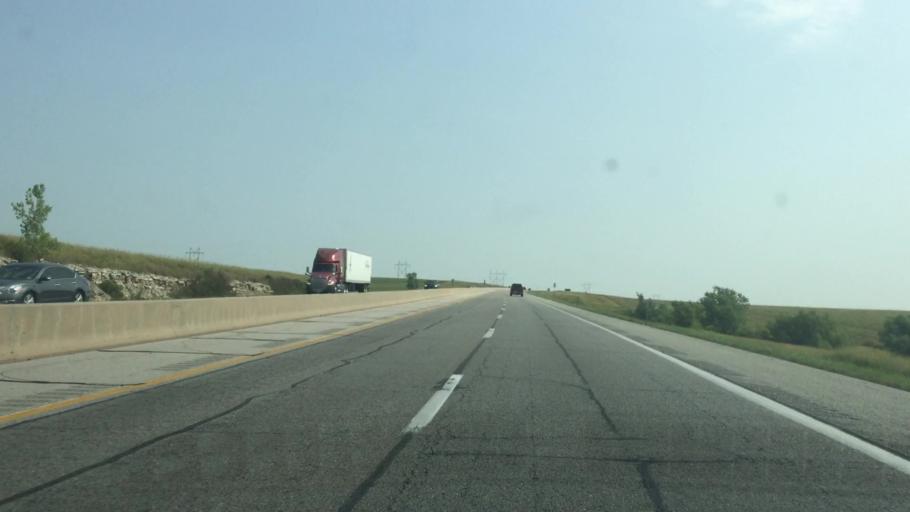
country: US
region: Kansas
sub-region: Chase County
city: Cottonwood Falls
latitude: 38.1795
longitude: -96.4630
